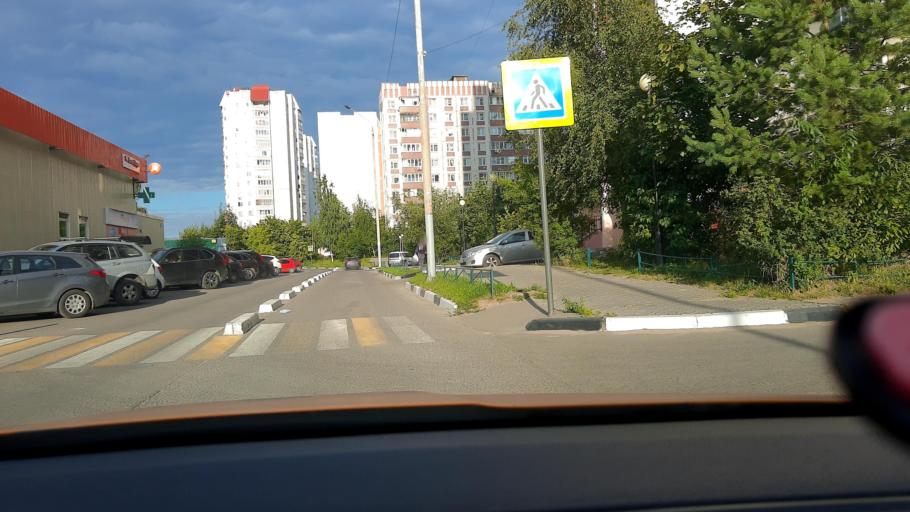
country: RU
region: Moskovskaya
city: Krasnoznamensk
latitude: 55.6037
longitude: 37.0272
